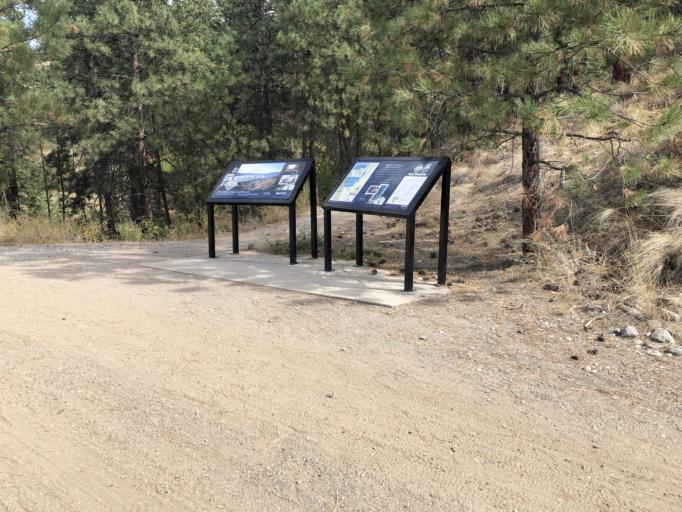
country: CA
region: British Columbia
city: Penticton
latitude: 49.5567
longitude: -119.5676
